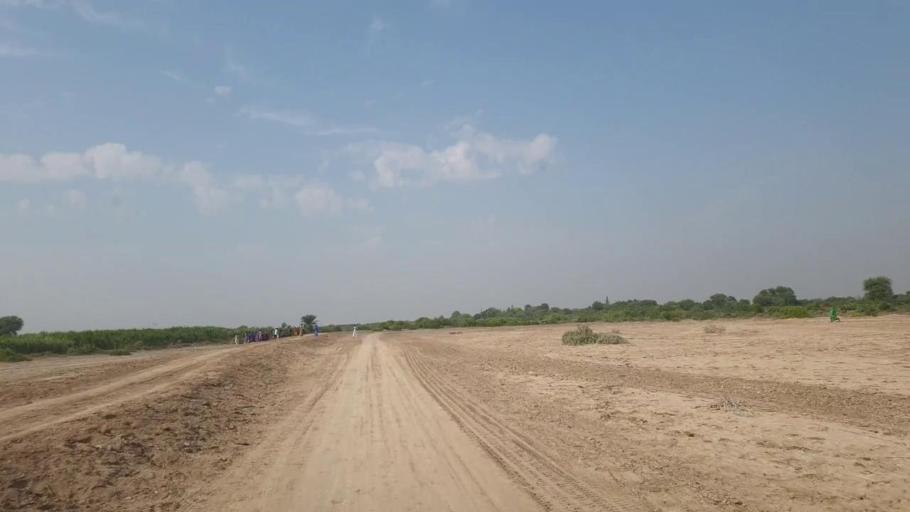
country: PK
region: Sindh
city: Digri
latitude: 25.0325
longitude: 69.0697
